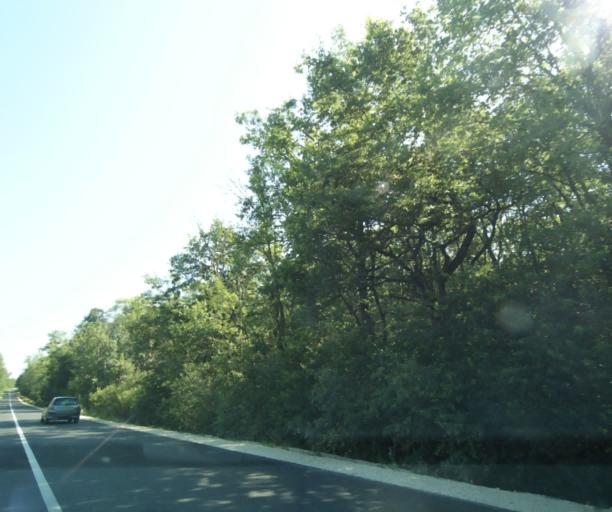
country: FR
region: Lorraine
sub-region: Departement de Meurthe-et-Moselle
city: Domgermain
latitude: 48.6397
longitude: 5.8645
